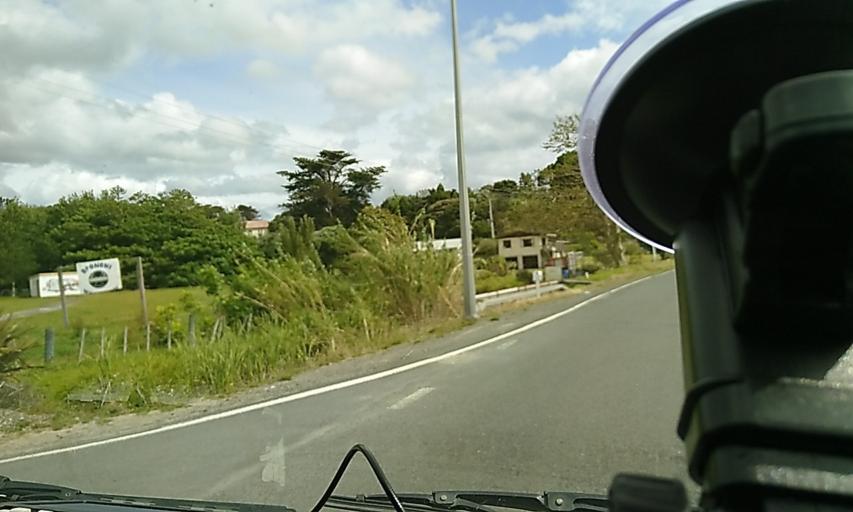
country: NZ
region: Northland
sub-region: Far North District
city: Ahipara
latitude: -35.5165
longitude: 173.3889
